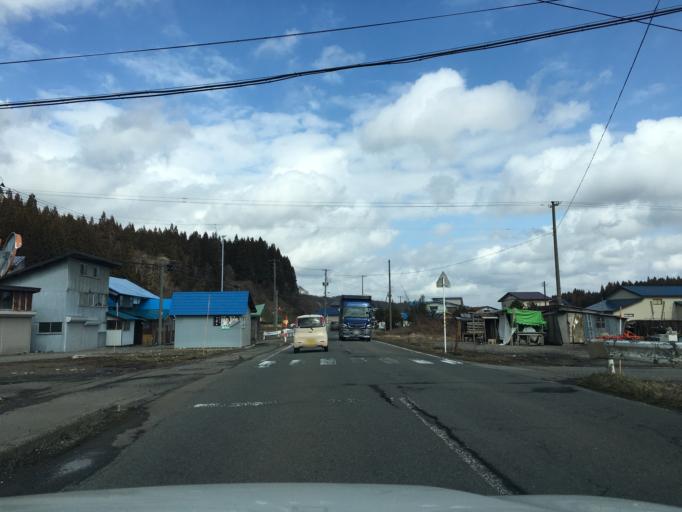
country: JP
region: Akita
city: Takanosu
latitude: 40.0332
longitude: 140.2750
